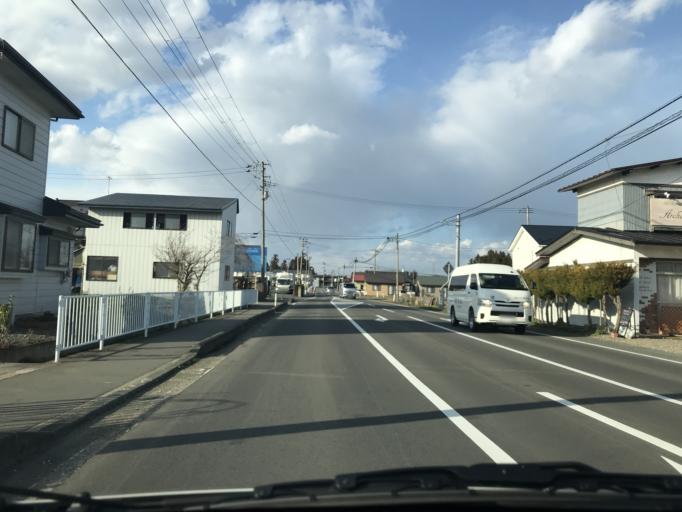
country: JP
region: Iwate
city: Kitakami
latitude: 39.3012
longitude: 141.0714
